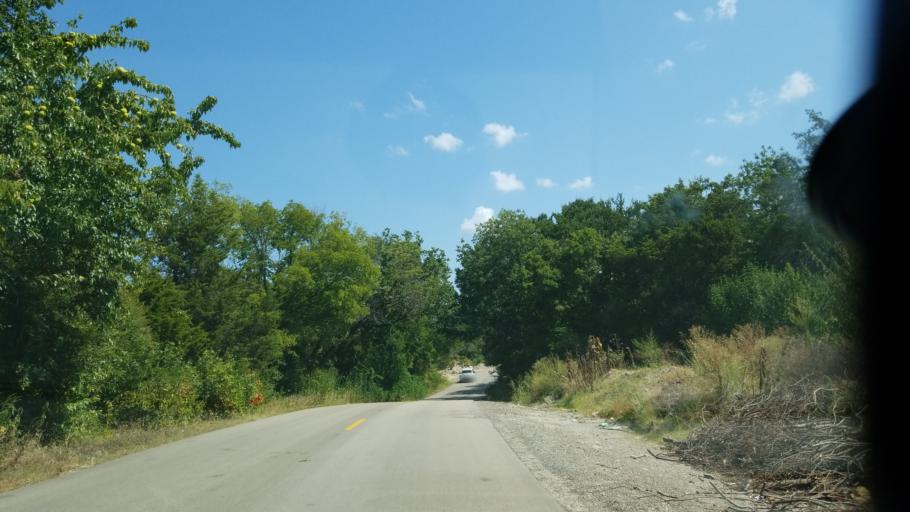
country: US
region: Texas
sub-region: Dallas County
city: Cockrell Hill
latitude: 32.7072
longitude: -96.9254
